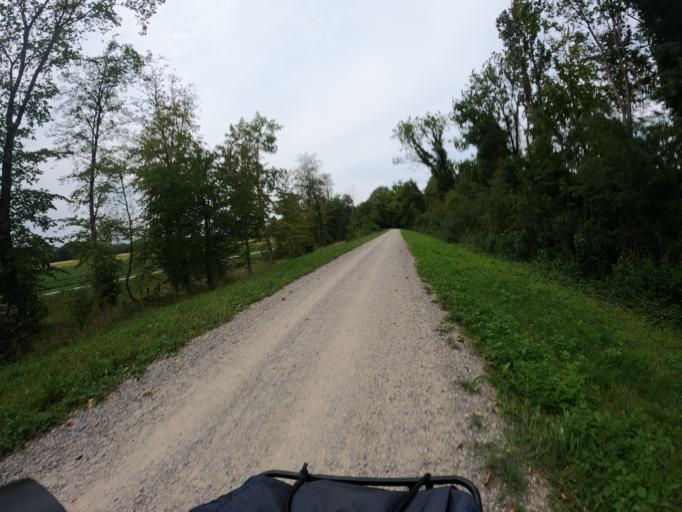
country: CH
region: Zurich
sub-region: Bezirk Affoltern
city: Ottenbach
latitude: 47.2693
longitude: 8.4006
